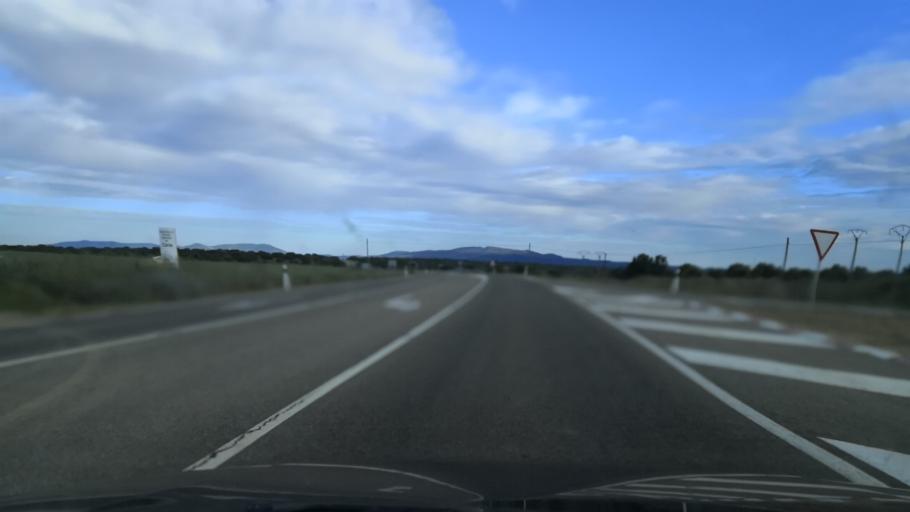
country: ES
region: Extremadura
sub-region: Provincia de Caceres
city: Torrejoncillo
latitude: 39.9302
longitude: -6.5042
